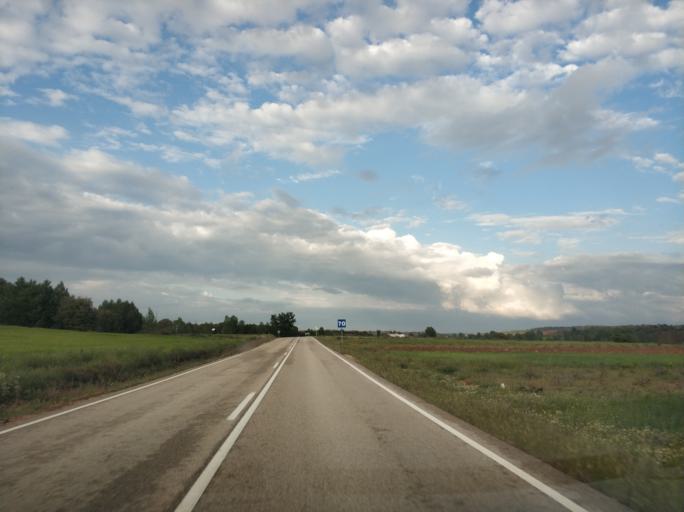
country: ES
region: Castille and Leon
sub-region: Provincia de Soria
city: Alcubilla de Avellaneda
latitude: 41.7221
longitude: -3.3304
